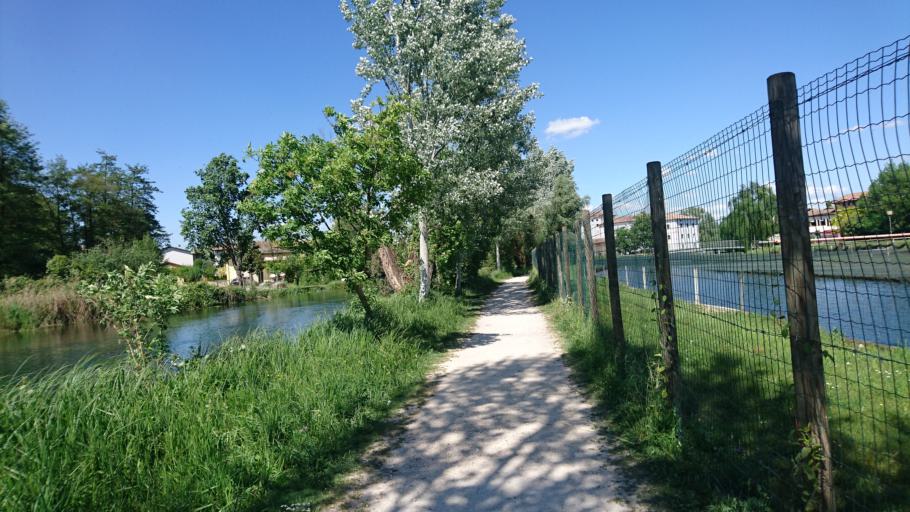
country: IT
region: Veneto
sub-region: Provincia di Treviso
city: Quinto di Treviso
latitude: 45.6435
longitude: 12.1606
